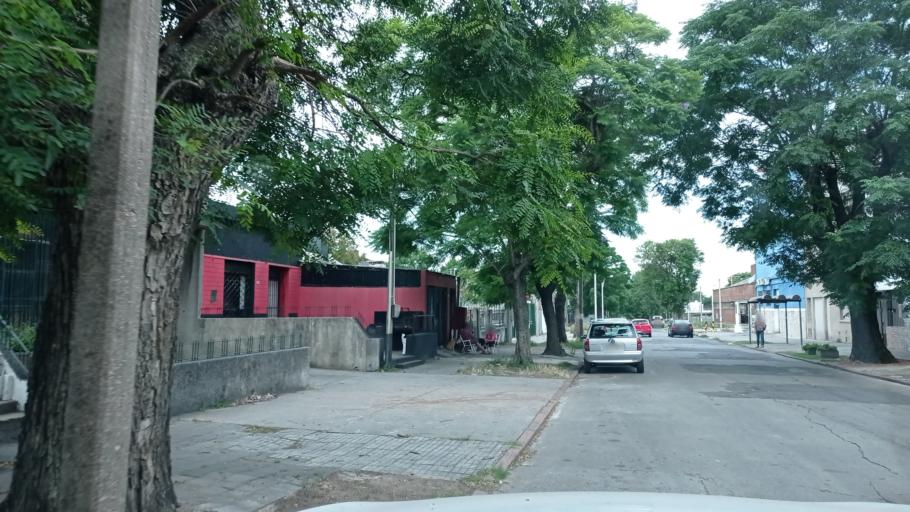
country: UY
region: Montevideo
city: Montevideo
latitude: -34.8703
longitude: -56.1571
